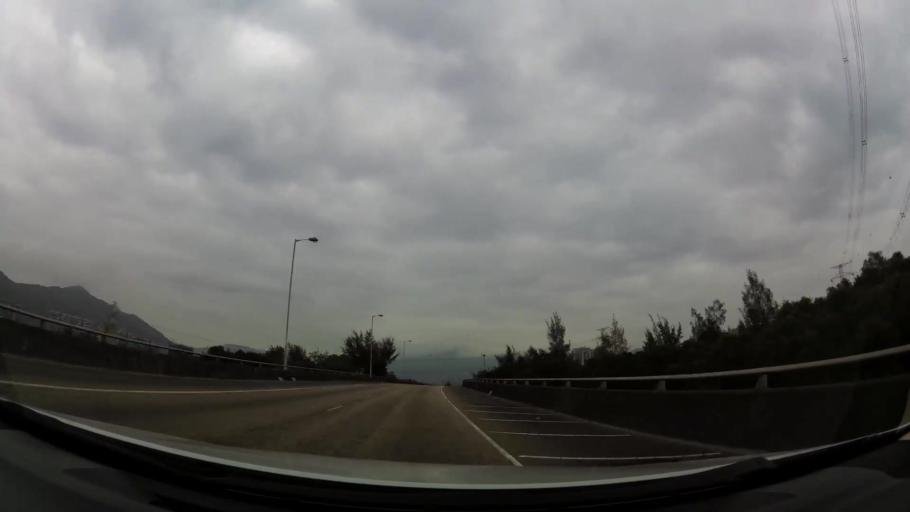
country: HK
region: Yuen Long
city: Yuen Long Kau Hui
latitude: 22.4492
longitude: 114.0474
